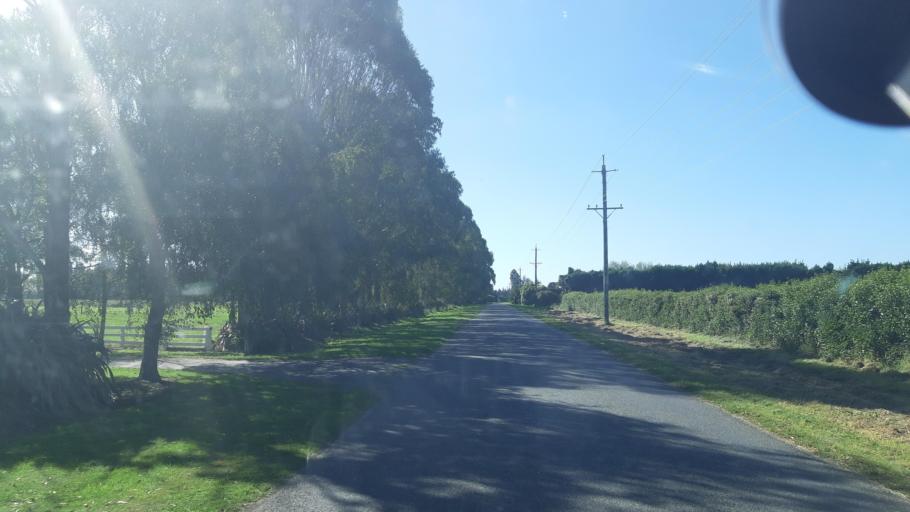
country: NZ
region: Canterbury
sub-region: Ashburton District
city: Ashburton
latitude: -43.9296
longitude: 171.7943
